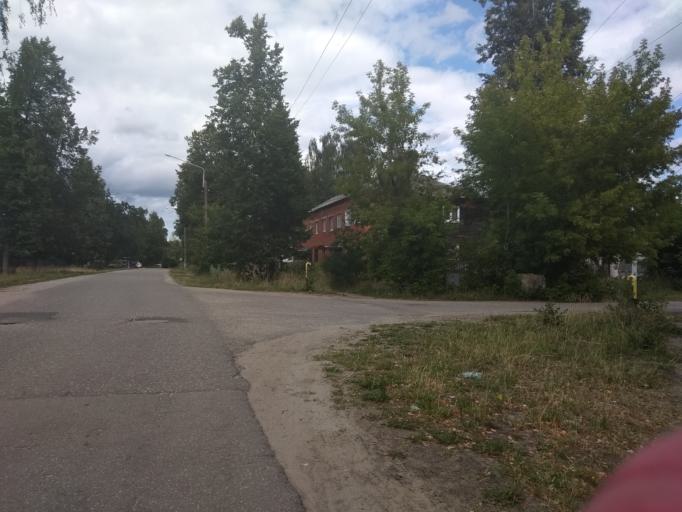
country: RU
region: Moskovskaya
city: Misheronskiy
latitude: 55.7191
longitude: 39.7389
